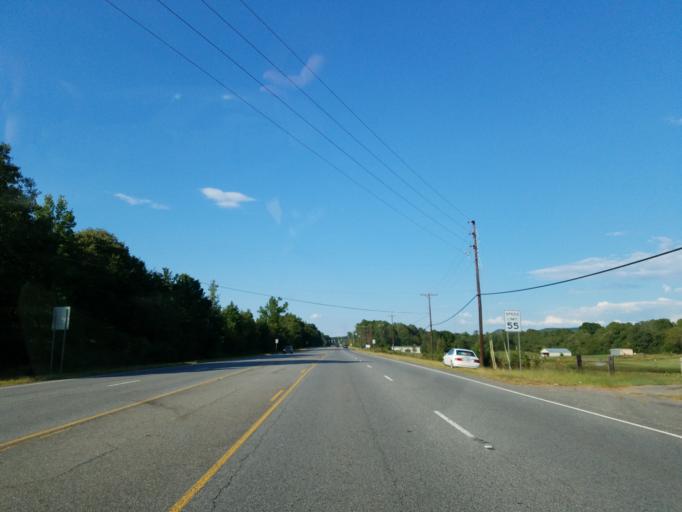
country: US
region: Georgia
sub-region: Murray County
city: Chatsworth
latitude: 34.8430
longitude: -84.7572
